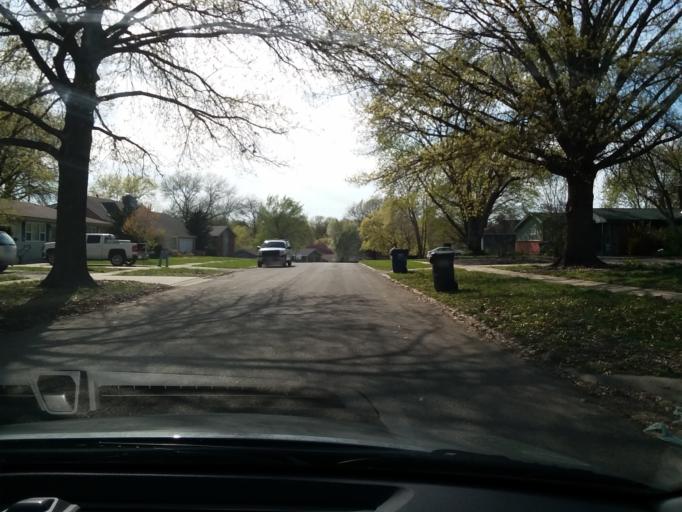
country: US
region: Kansas
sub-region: Douglas County
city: Lawrence
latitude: 38.9700
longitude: -95.2721
